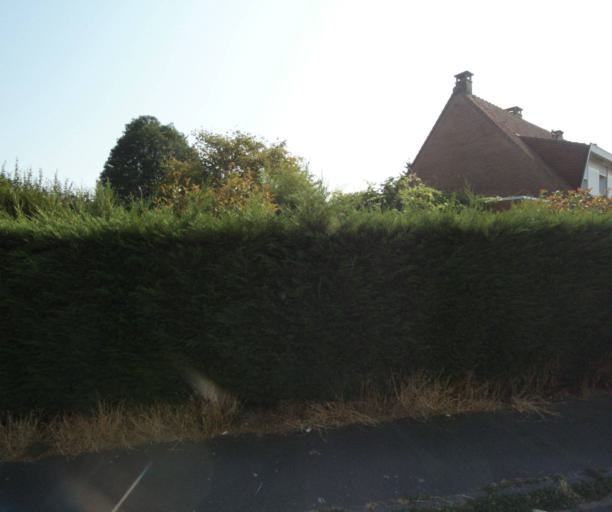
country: FR
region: Nord-Pas-de-Calais
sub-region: Departement du Nord
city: Quesnoy-sur-Deule
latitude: 50.7184
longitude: 2.9959
